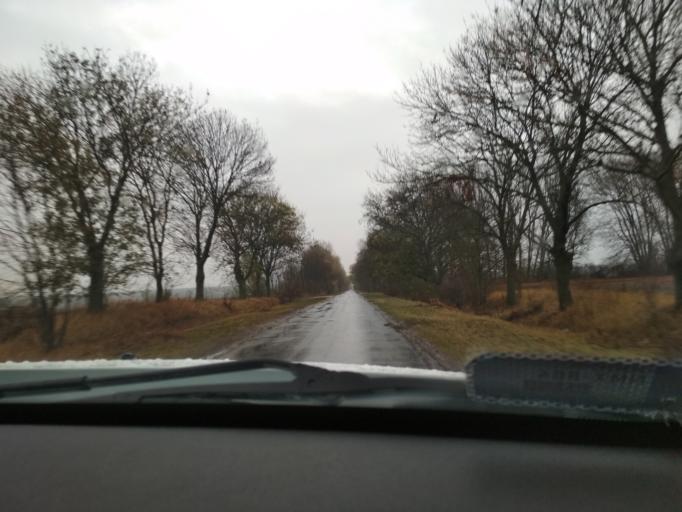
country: HU
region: Csongrad
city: Baks
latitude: 46.5399
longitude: 20.1338
